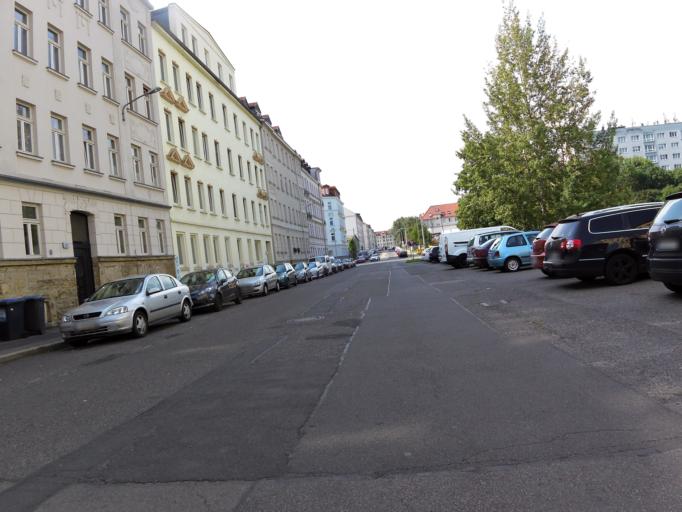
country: DE
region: Saxony
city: Leipzig
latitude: 51.3700
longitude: 12.3400
